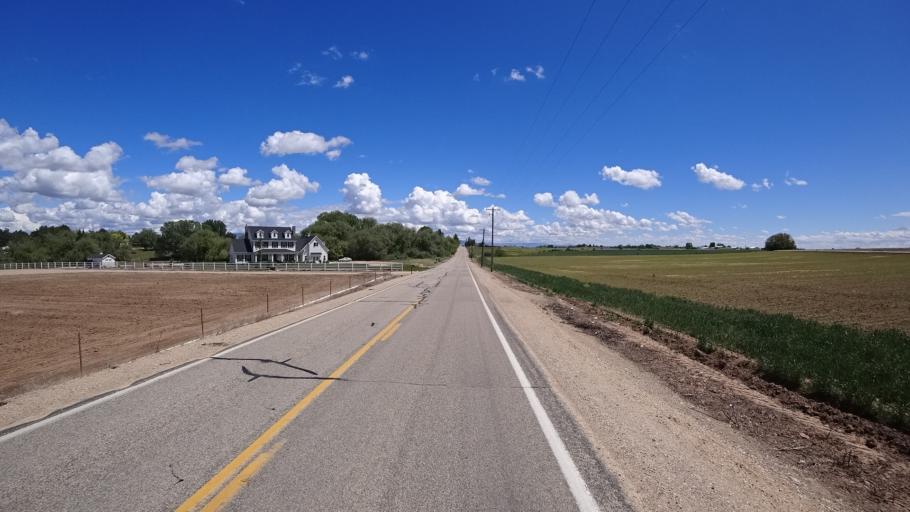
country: US
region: Idaho
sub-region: Ada County
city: Meridian
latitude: 43.5903
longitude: -116.4619
